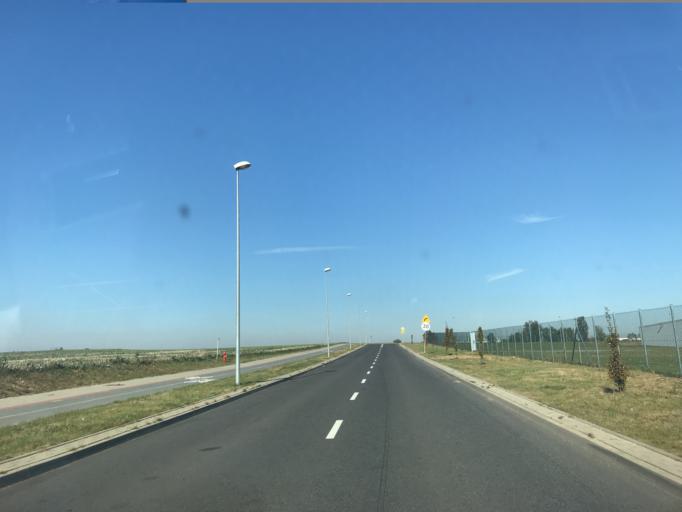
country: PL
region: Warmian-Masurian Voivodeship
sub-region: Powiat ilawski
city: Lubawa
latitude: 53.5141
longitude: 19.7255
